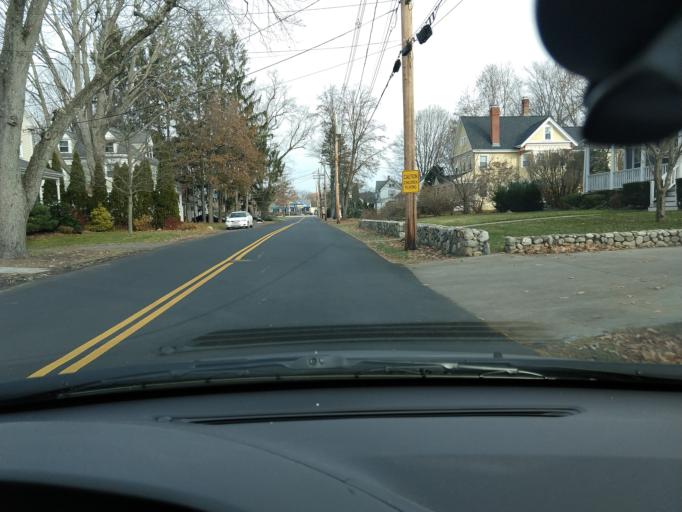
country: US
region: Massachusetts
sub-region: Middlesex County
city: Bedford
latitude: 42.4882
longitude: -71.2742
